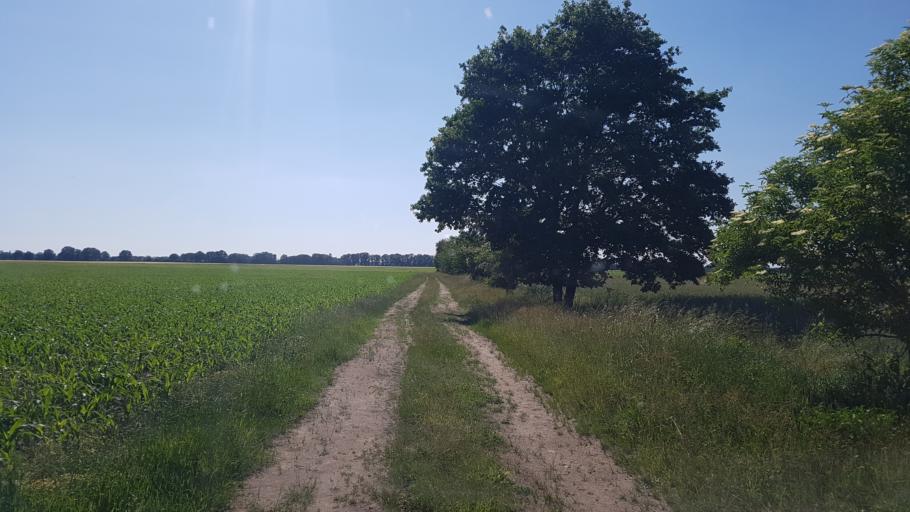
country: DE
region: Brandenburg
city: Sonnewalde
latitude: 51.6845
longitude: 13.6805
